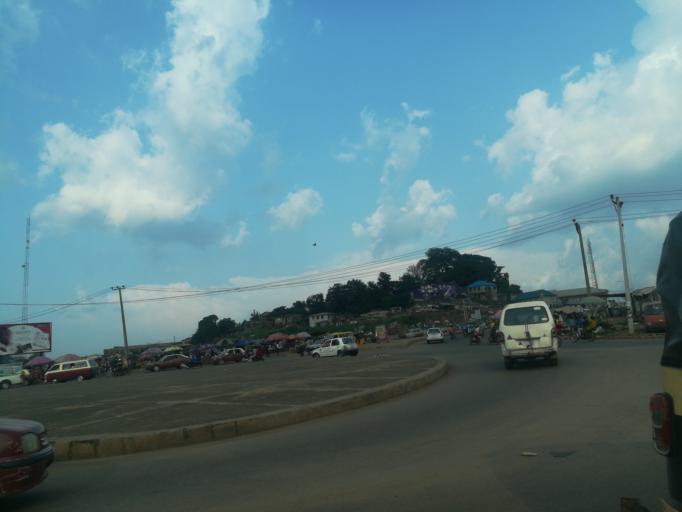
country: NG
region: Oyo
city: Moniya
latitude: 7.4715
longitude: 3.9131
